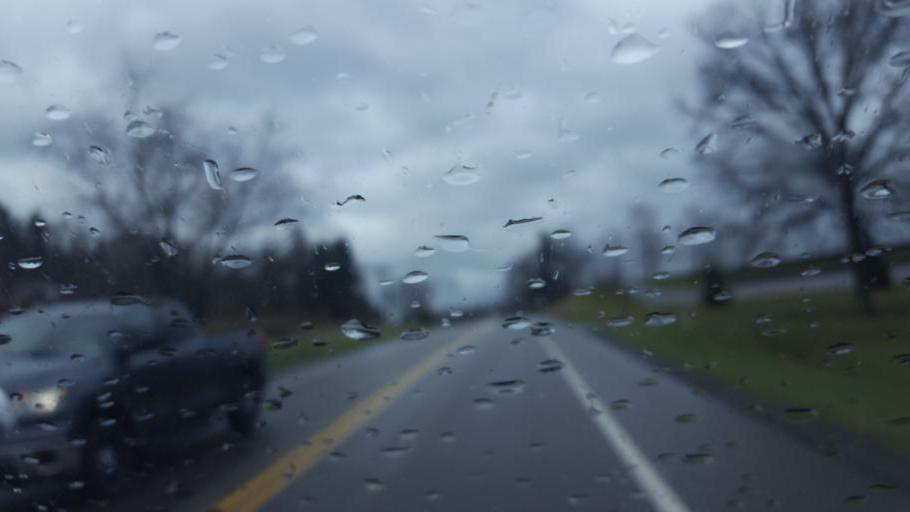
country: US
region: Ohio
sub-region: Holmes County
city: Millersburg
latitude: 40.5554
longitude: -81.9040
